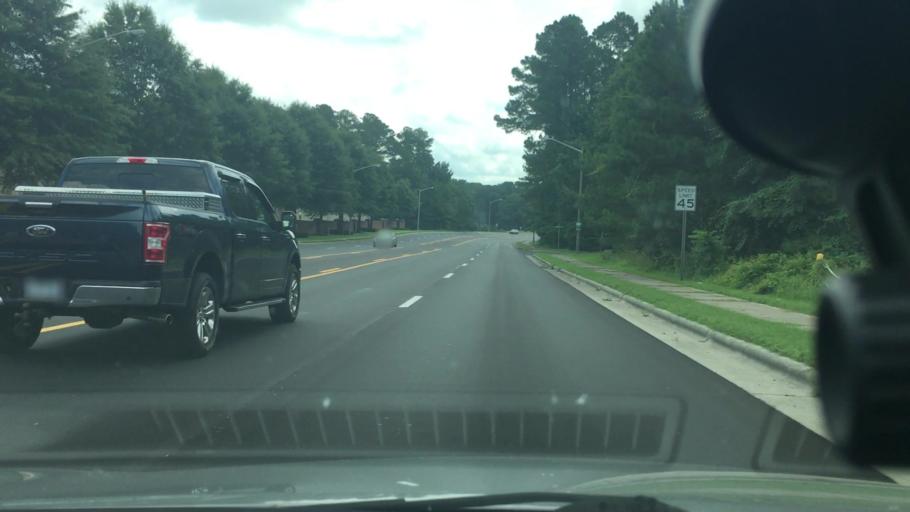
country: US
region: North Carolina
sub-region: Pitt County
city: Greenville
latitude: 35.5933
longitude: -77.3208
